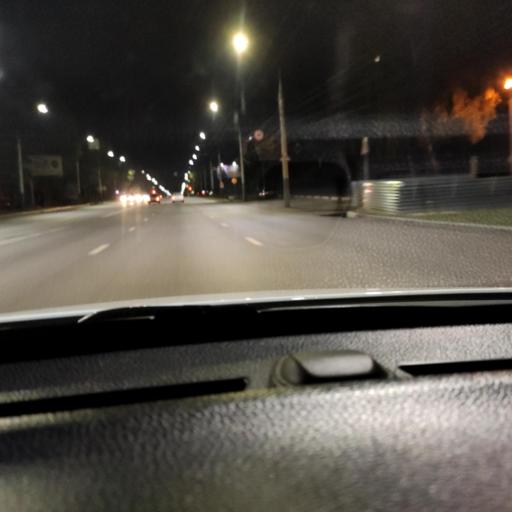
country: RU
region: Voronezj
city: Voronezh
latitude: 51.6586
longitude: 39.2455
